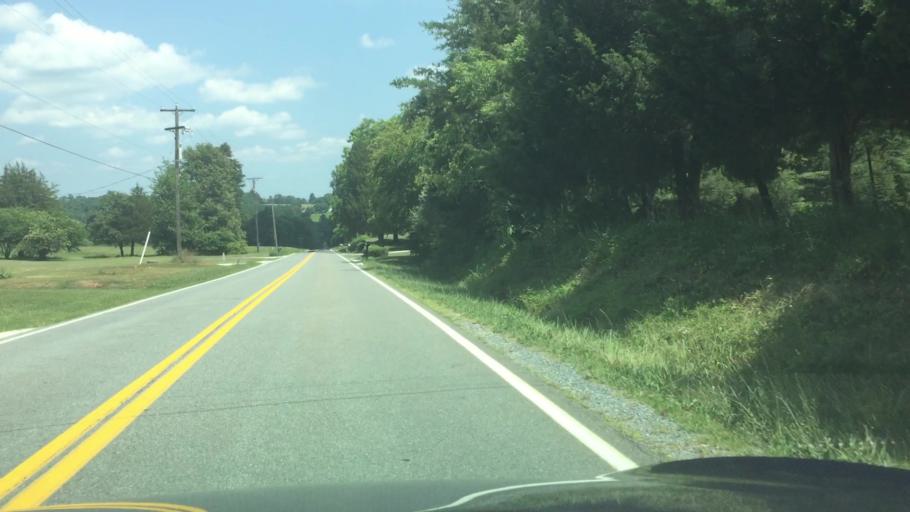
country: US
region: Virginia
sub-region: Appomattox County
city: Appomattox
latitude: 37.3422
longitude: -78.8978
